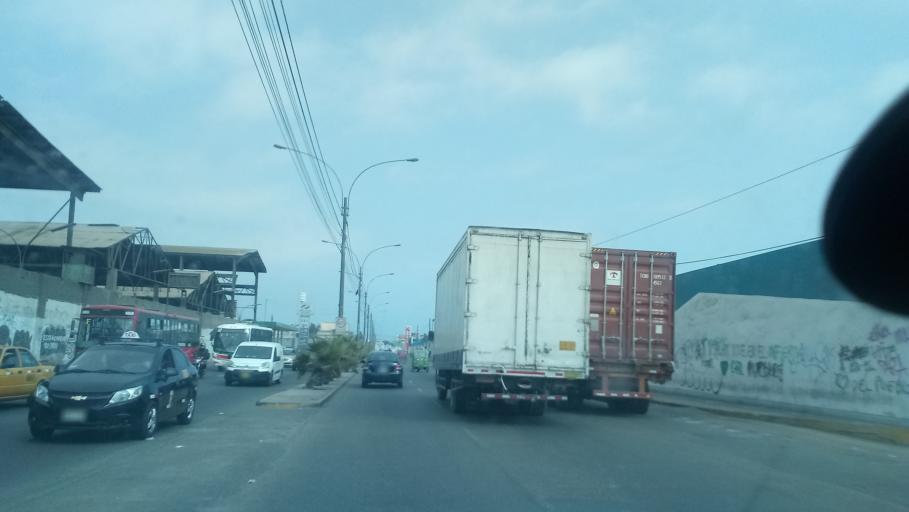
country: PE
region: Callao
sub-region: Callao
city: Callao
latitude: -12.0390
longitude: -77.0774
